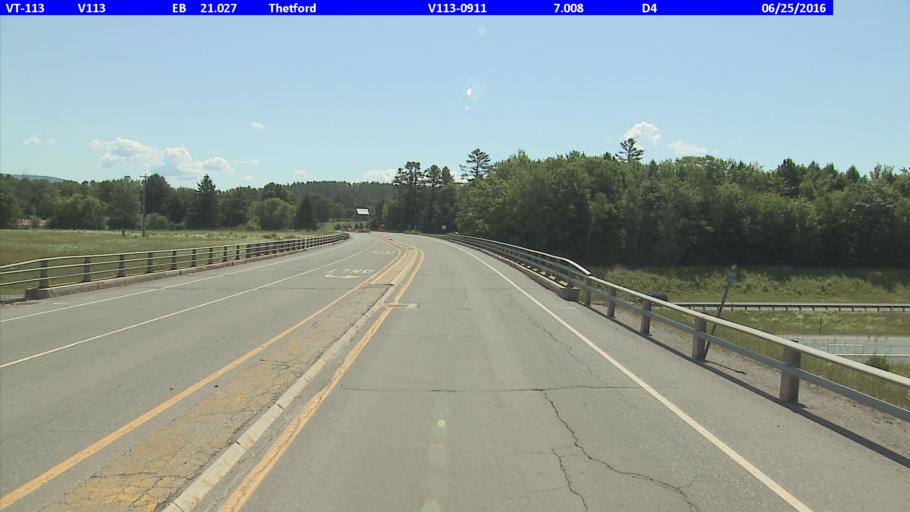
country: US
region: New Hampshire
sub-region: Grafton County
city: Lyme
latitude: 43.8129
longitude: -72.2170
